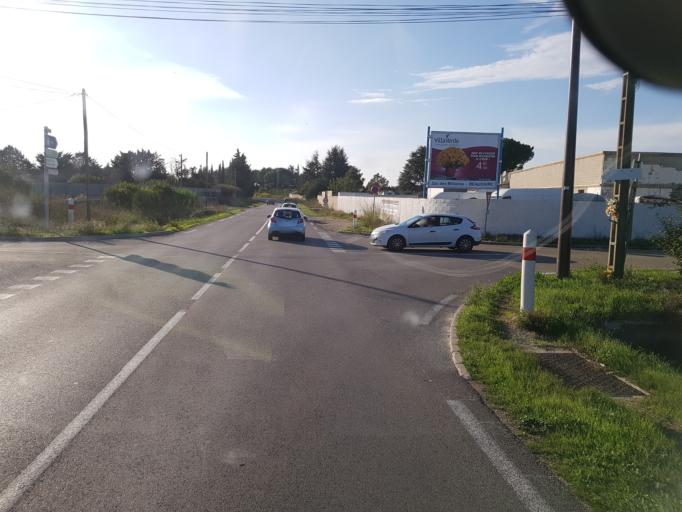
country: FR
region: Languedoc-Roussillon
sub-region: Departement du Gard
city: Redessan
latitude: 43.8271
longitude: 4.5064
